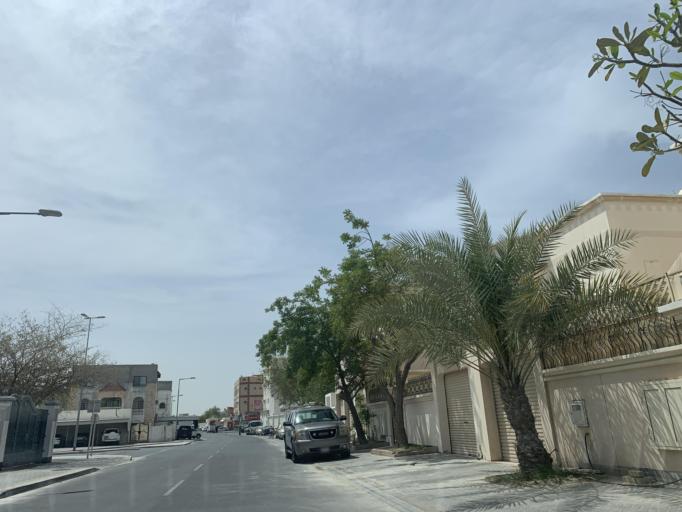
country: BH
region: Northern
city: Ar Rifa'
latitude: 26.1441
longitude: 50.5639
